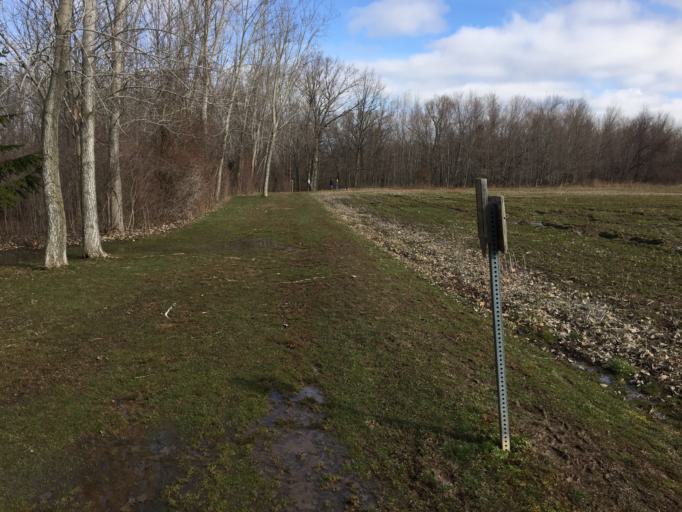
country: US
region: New York
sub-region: Monroe County
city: Hilton
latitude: 43.2536
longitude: -77.7811
